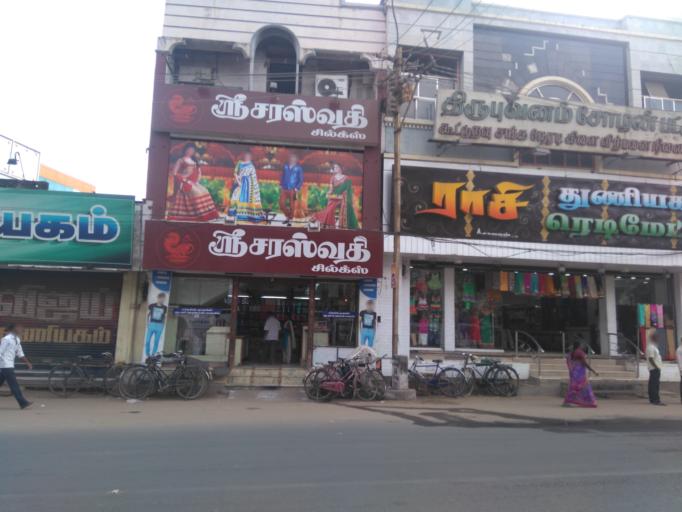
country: IN
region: Tamil Nadu
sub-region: Thanjavur
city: Thanjavur
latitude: 10.7854
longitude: 79.1388
